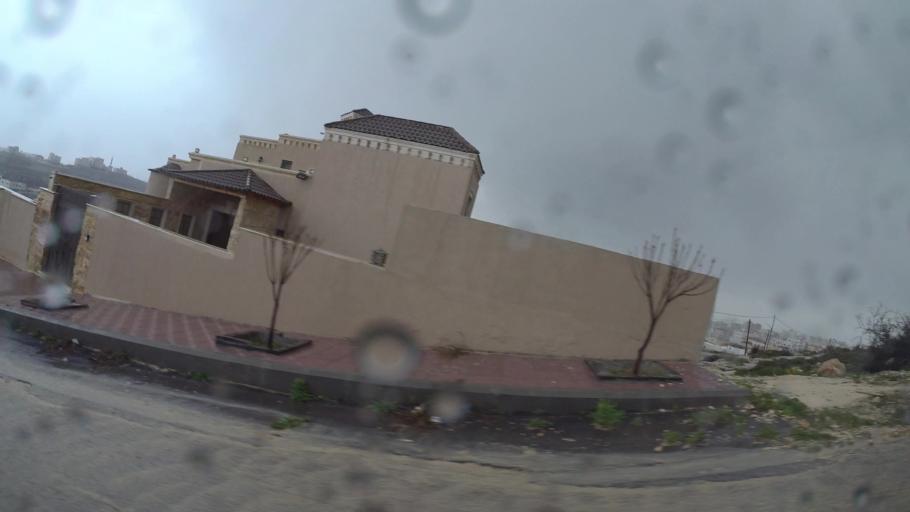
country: JO
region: Amman
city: Umm as Summaq
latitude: 31.8753
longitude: 35.8612
